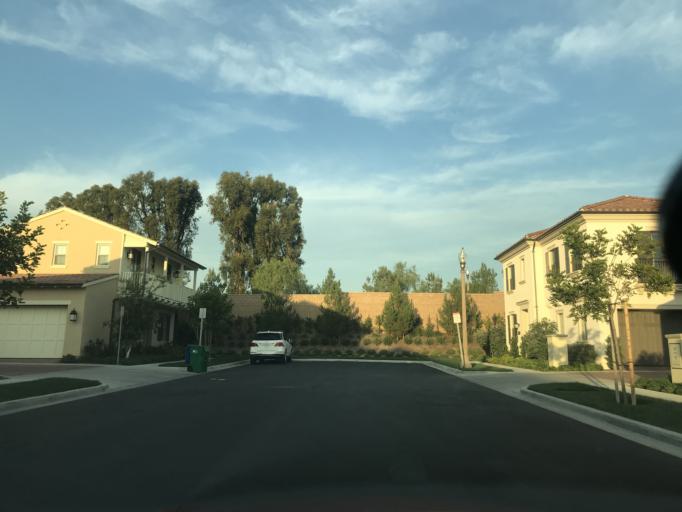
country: US
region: California
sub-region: Orange County
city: North Tustin
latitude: 33.7129
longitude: -117.7465
